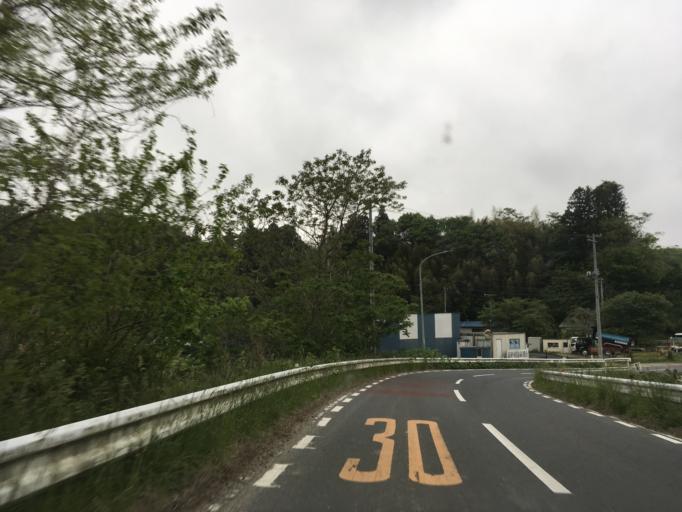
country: JP
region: Miyagi
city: Wakuya
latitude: 38.7147
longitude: 141.2946
